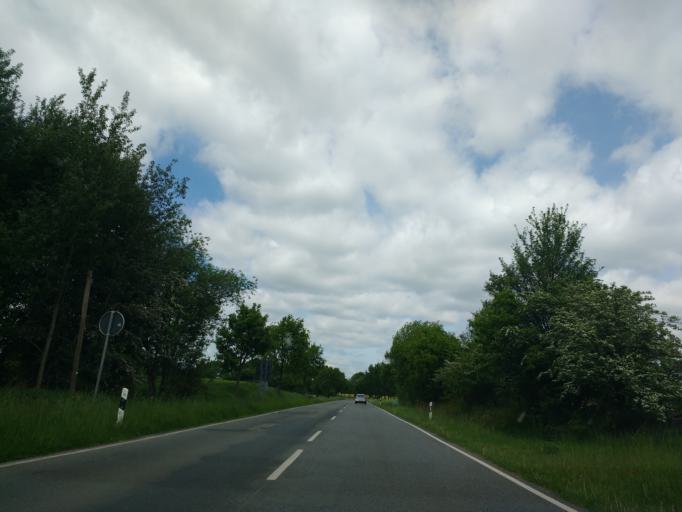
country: DE
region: Schleswig-Holstein
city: Braak
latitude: 53.5880
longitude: 10.2480
